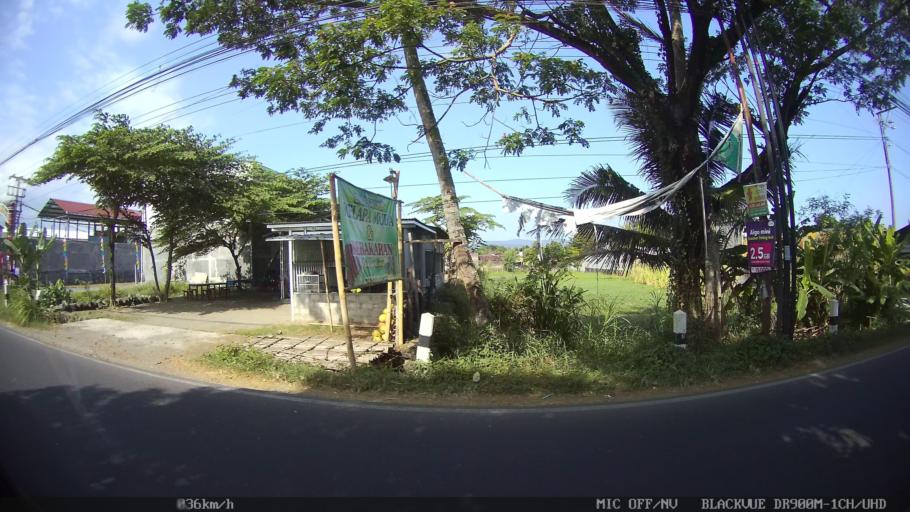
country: ID
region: Daerah Istimewa Yogyakarta
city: Sewon
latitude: -7.8575
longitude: 110.3898
